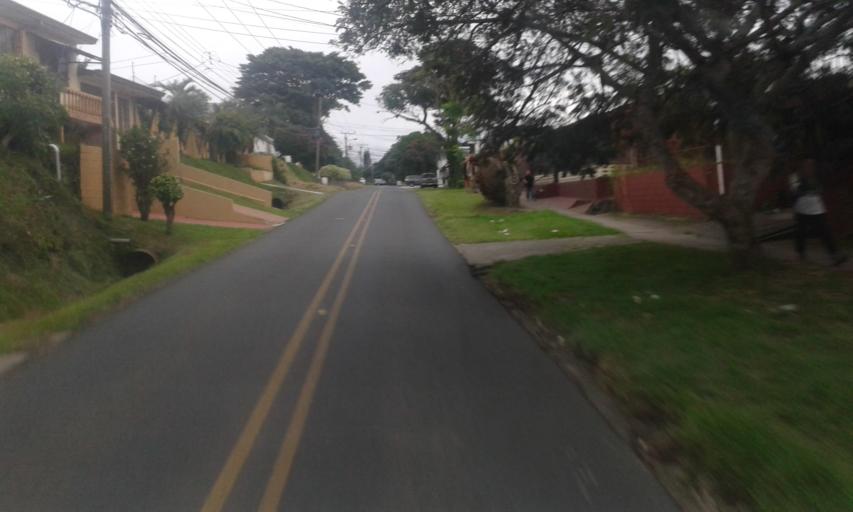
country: CR
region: San Jose
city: San Juan
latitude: 9.9780
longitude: -84.0850
